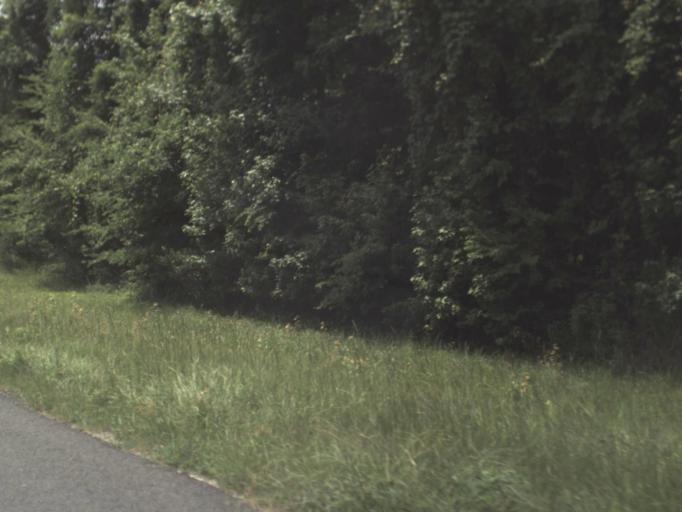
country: US
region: Florida
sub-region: Hamilton County
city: Jasper
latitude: 30.4816
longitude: -82.9193
